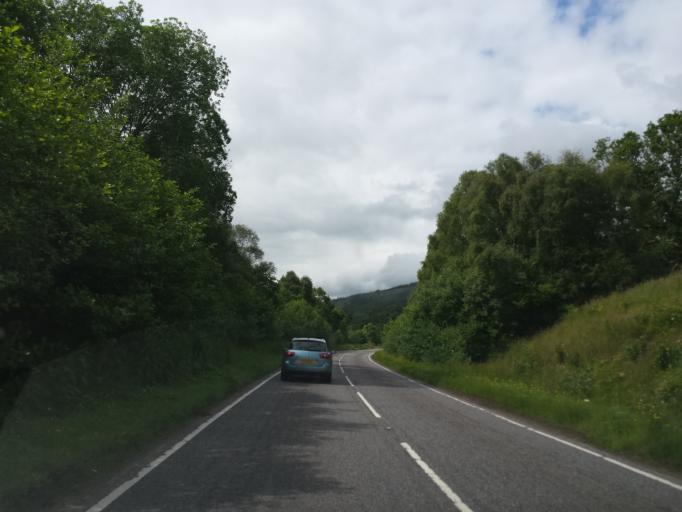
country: GB
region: Scotland
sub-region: Highland
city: Fort William
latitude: 56.8509
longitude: -5.1700
